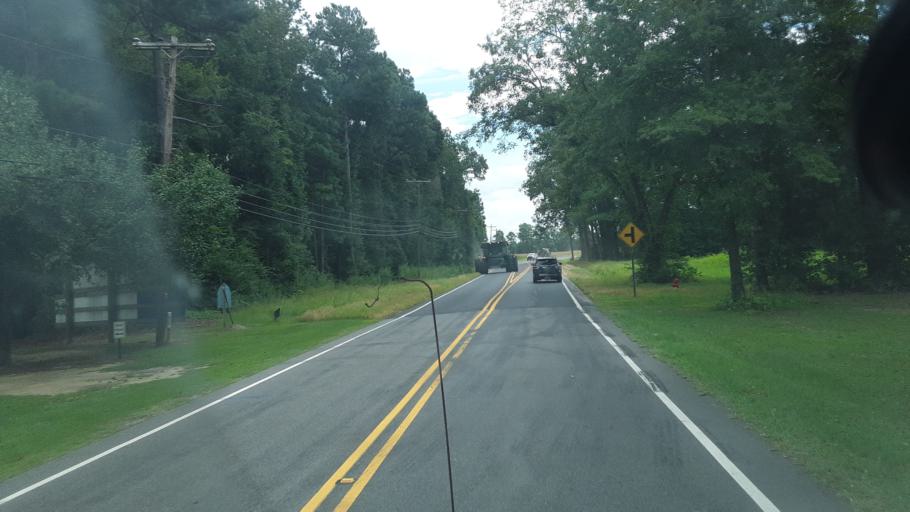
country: US
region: North Carolina
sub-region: Robeson County
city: Rowland
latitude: 34.5329
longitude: -79.2831
